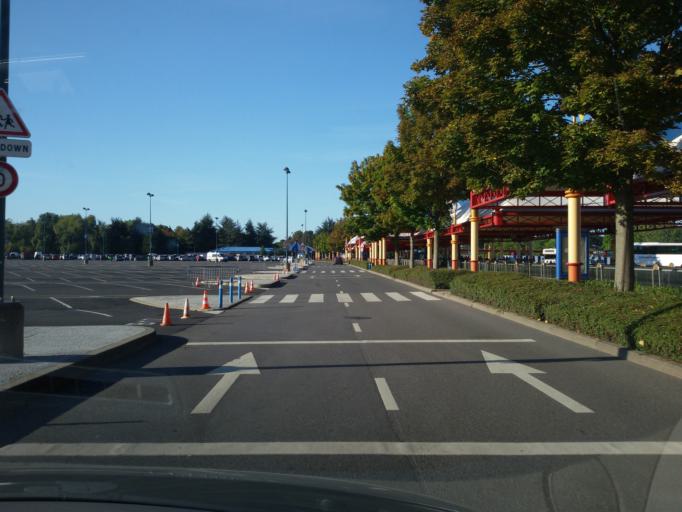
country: FR
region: Ile-de-France
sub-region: Departement de Seine-et-Marne
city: Chalifert
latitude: 48.8749
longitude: 2.7868
